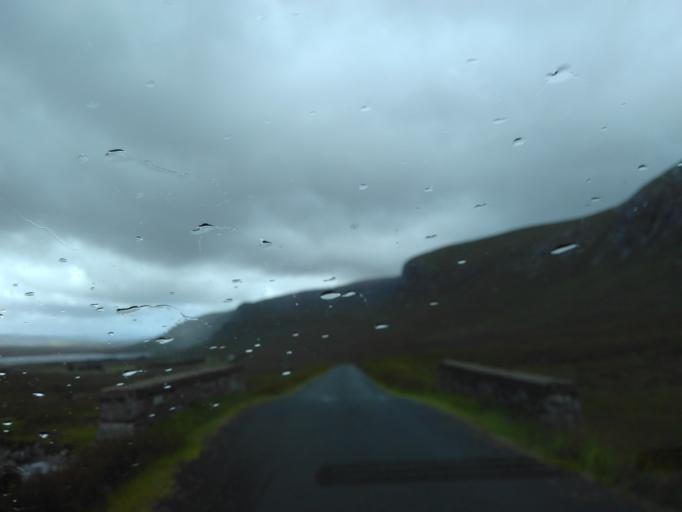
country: IE
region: Ulster
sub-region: County Donegal
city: Dunlewy
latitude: 54.9730
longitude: -8.0812
